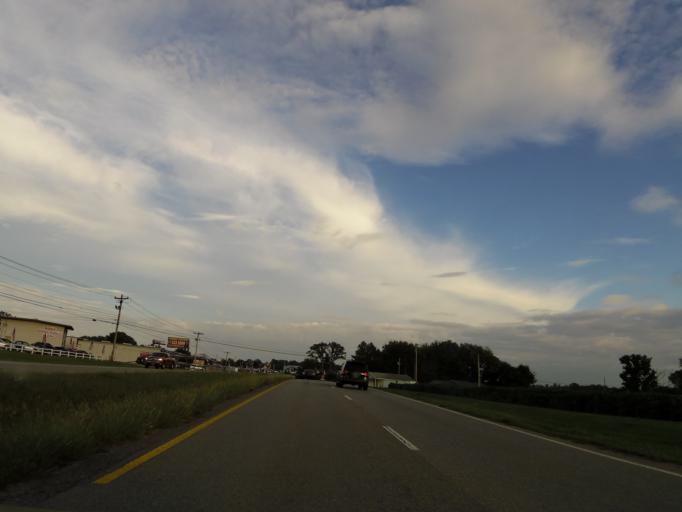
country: US
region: Alabama
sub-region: Limestone County
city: Athens
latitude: 34.7679
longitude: -86.8963
